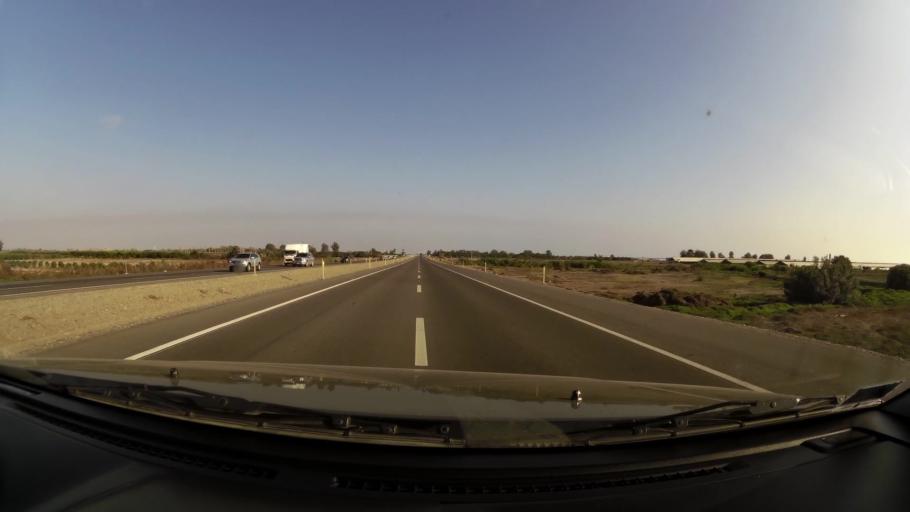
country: PE
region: Ica
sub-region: Provincia de Chincha
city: Chincha Baja
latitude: -13.4846
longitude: -76.1847
